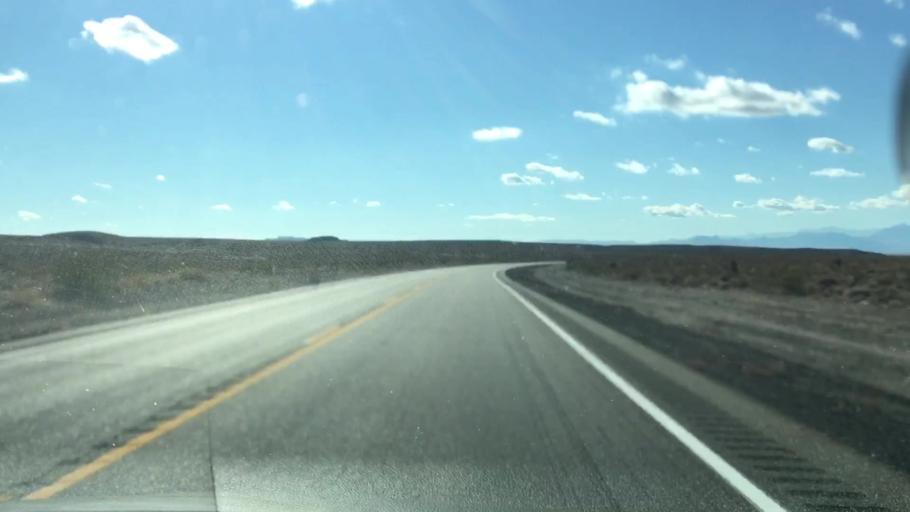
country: US
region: Nevada
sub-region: Nye County
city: Pahrump
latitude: 36.5655
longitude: -116.0839
